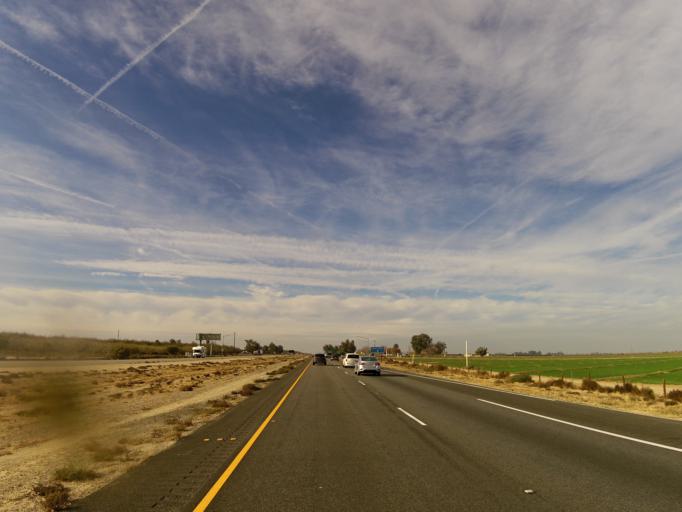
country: US
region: California
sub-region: Kern County
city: Buttonwillow
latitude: 35.4142
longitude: -119.4180
